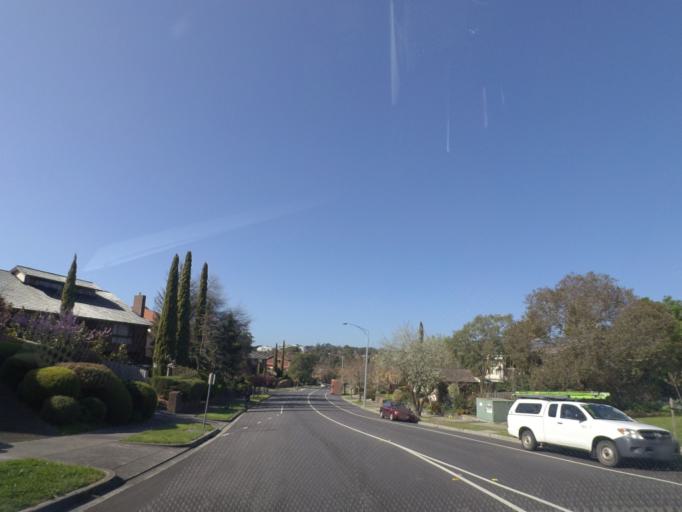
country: AU
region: Victoria
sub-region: Manningham
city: Doncaster East
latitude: -37.7679
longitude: 145.1594
